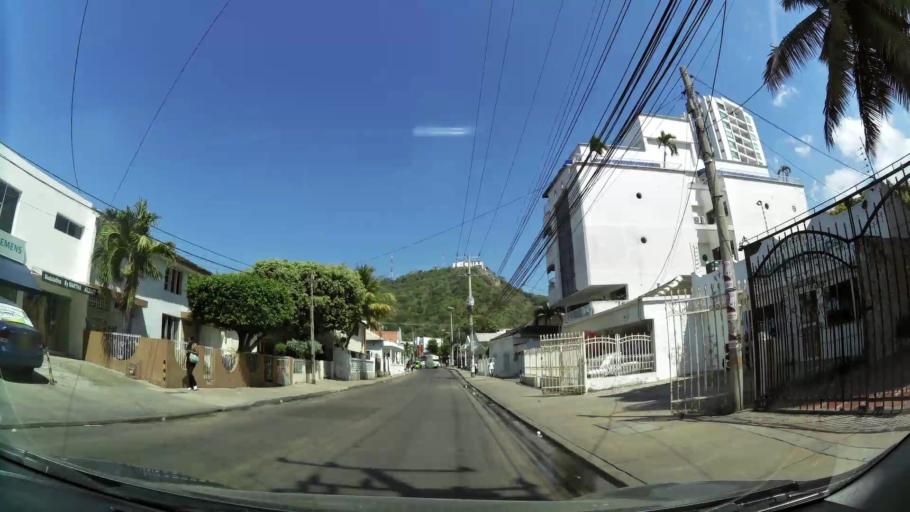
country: CO
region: Bolivar
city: Cartagena
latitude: 10.4157
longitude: -75.5308
